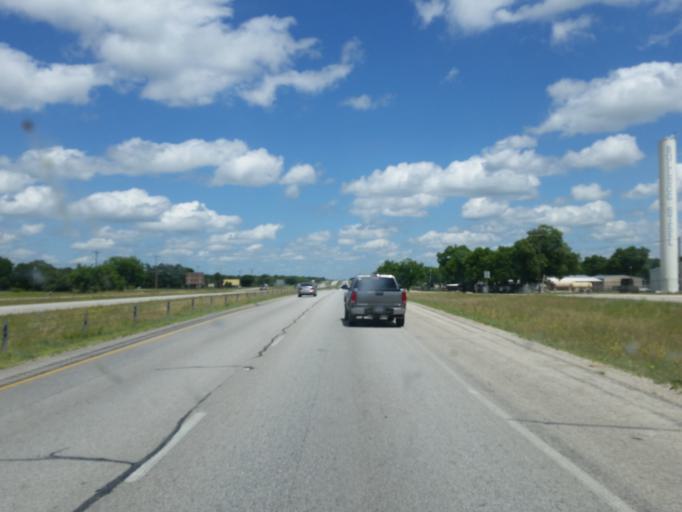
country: US
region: Texas
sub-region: Callahan County
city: Clyde
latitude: 32.4110
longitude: -99.4834
